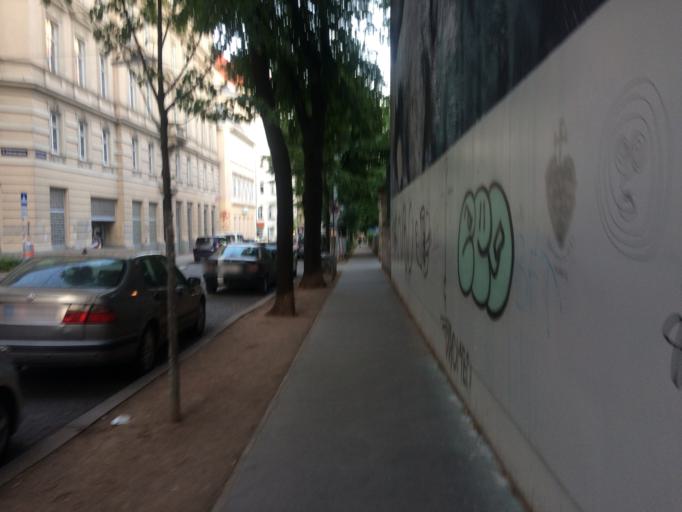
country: AT
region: Vienna
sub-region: Wien Stadt
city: Vienna
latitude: 48.1981
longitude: 16.3514
